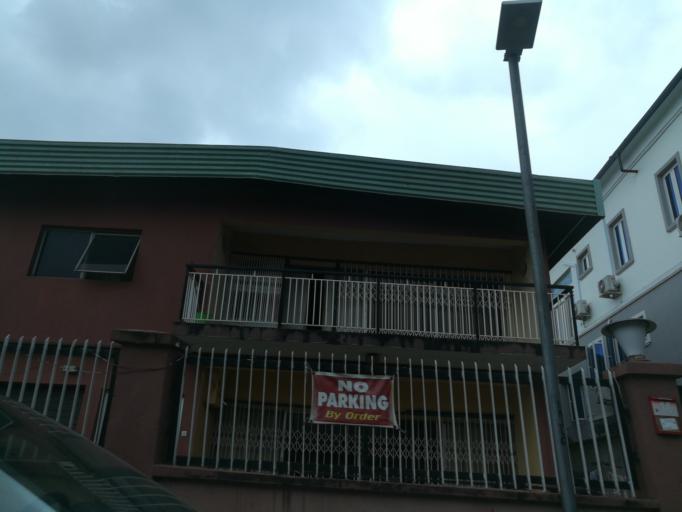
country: NG
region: Lagos
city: Ikeja
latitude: 6.6015
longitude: 3.3476
